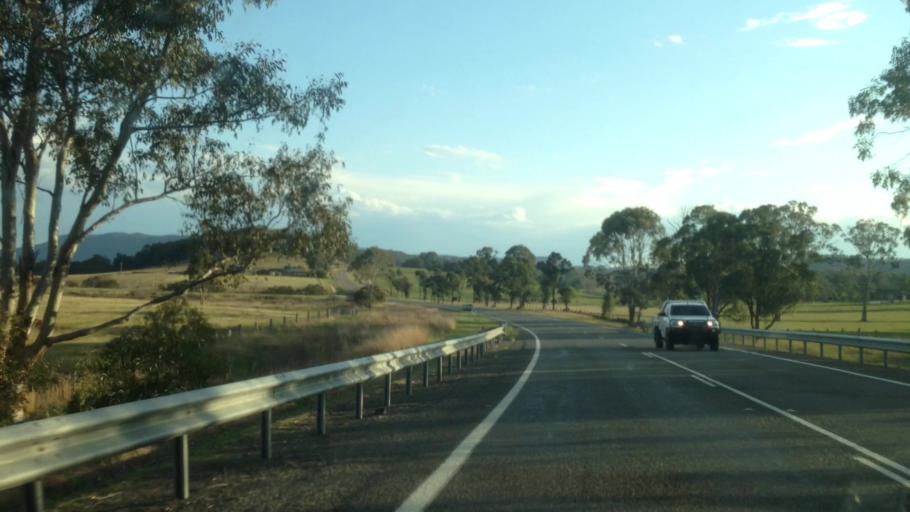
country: AU
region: New South Wales
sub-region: Cessnock
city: Kurri Kurri
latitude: -32.8743
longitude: 151.4760
